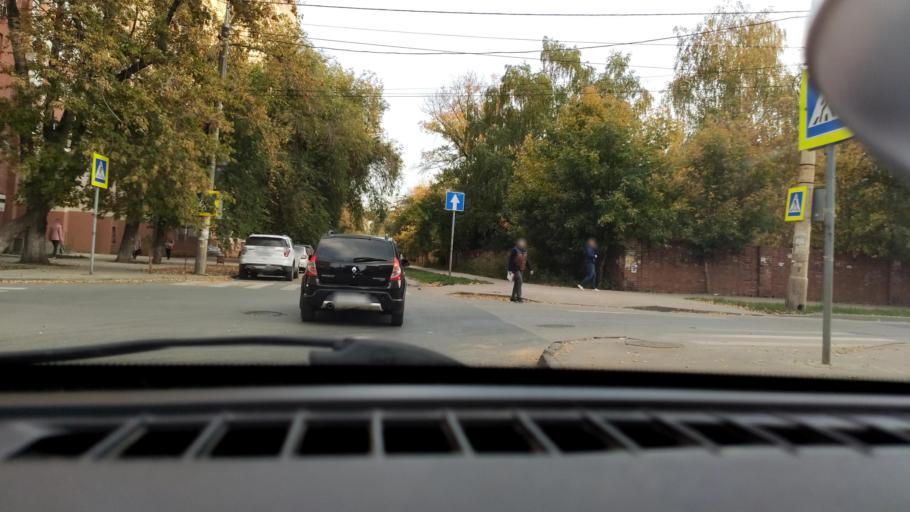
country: RU
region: Samara
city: Samara
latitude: 53.2104
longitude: 50.1615
